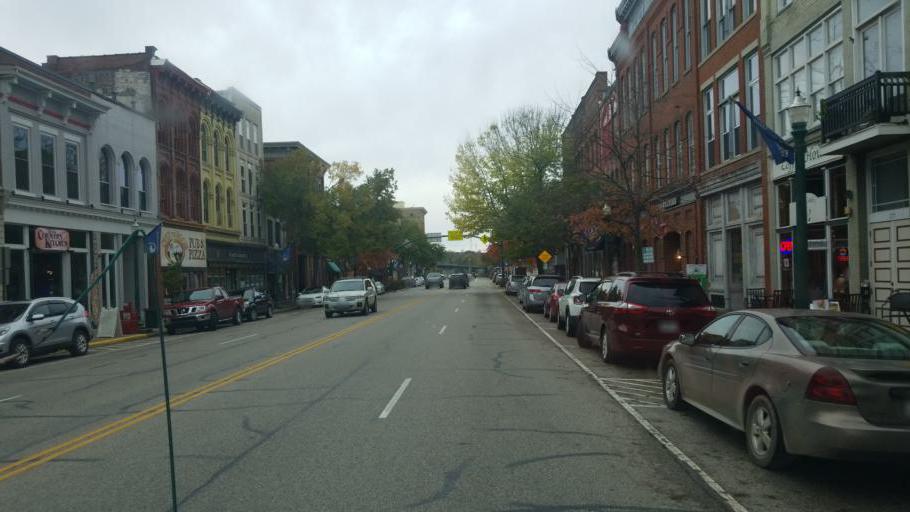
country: US
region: Ohio
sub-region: Washington County
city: Marietta
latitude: 39.4122
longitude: -81.4538
